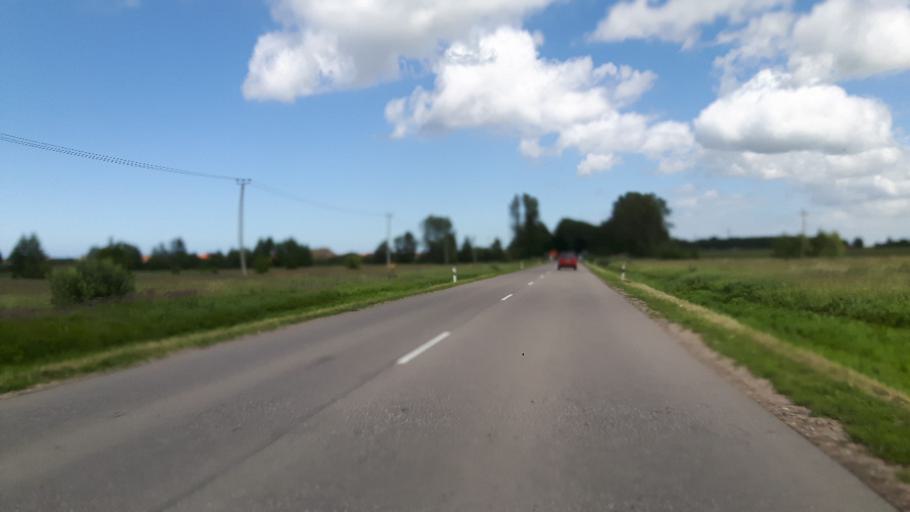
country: RU
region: Kaliningrad
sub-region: Zelenogradskiy Rayon
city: Zelenogradsk
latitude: 54.9331
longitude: 20.4346
